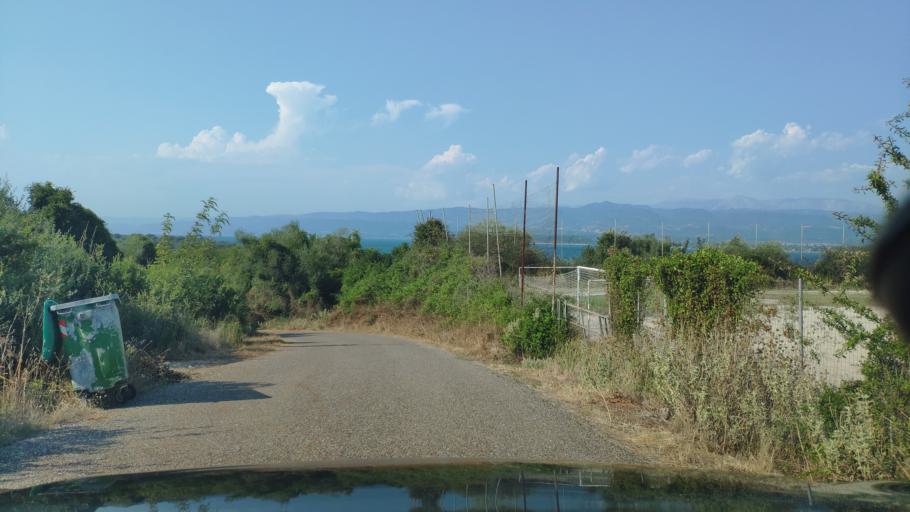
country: GR
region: West Greece
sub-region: Nomos Aitolias kai Akarnanias
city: Amfilochia
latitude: 38.9027
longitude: 21.1124
